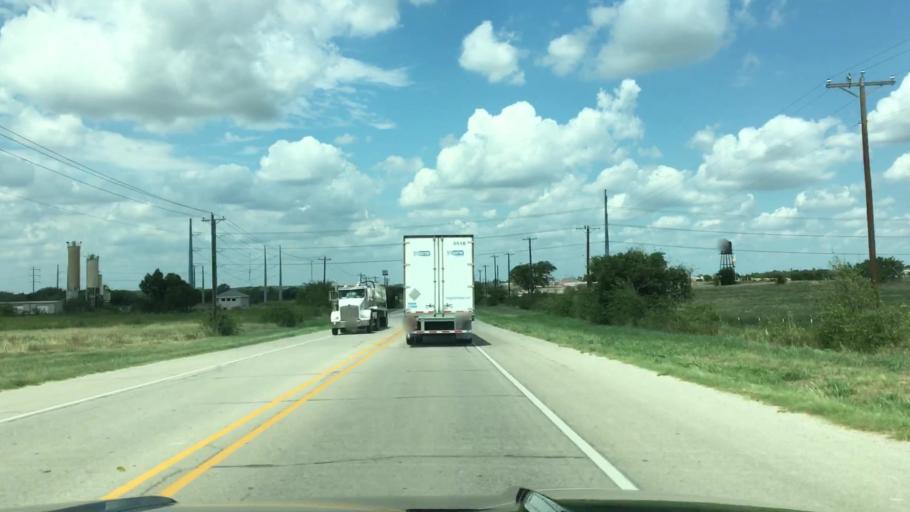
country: US
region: Texas
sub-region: Tarrant County
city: Pecan Acres
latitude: 32.9604
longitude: -97.4208
